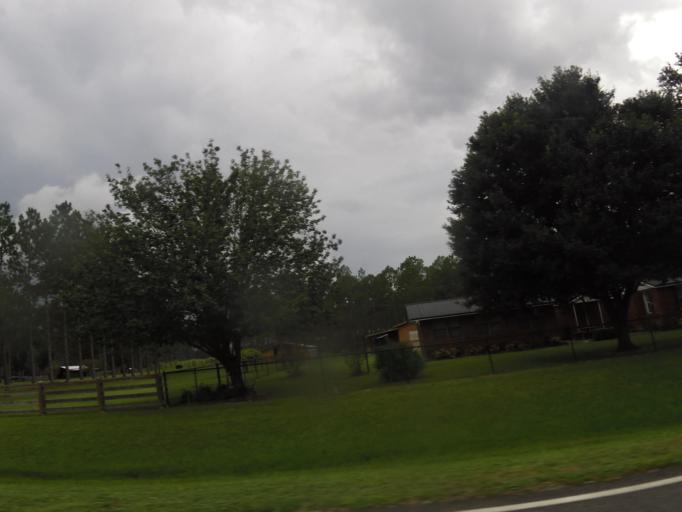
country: US
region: Florida
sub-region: Baker County
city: Macclenny
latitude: 30.4564
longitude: -82.1979
